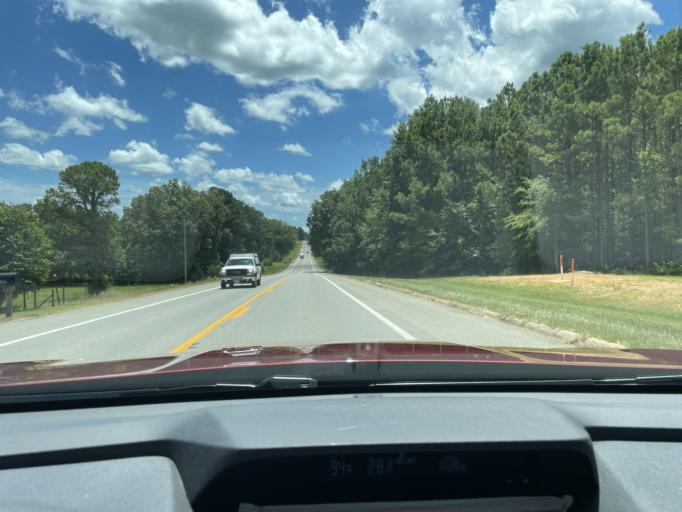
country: US
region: Arkansas
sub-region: Drew County
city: Monticello
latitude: 33.7379
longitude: -91.8188
